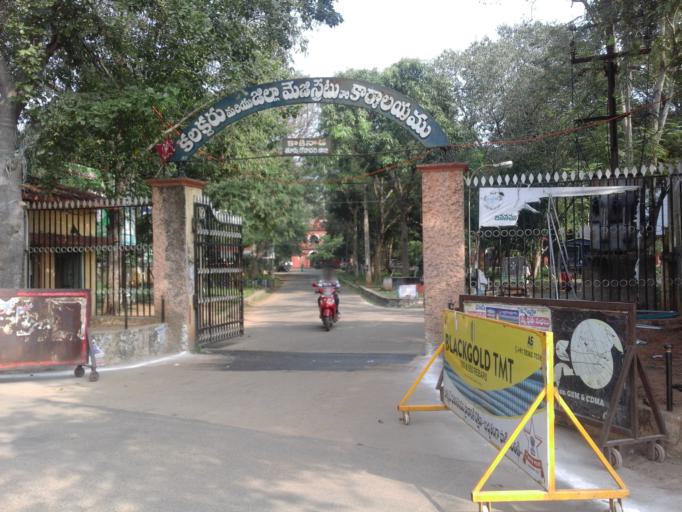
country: IN
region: Andhra Pradesh
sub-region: East Godavari
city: Kakinada
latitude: 16.9589
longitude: 82.2258
